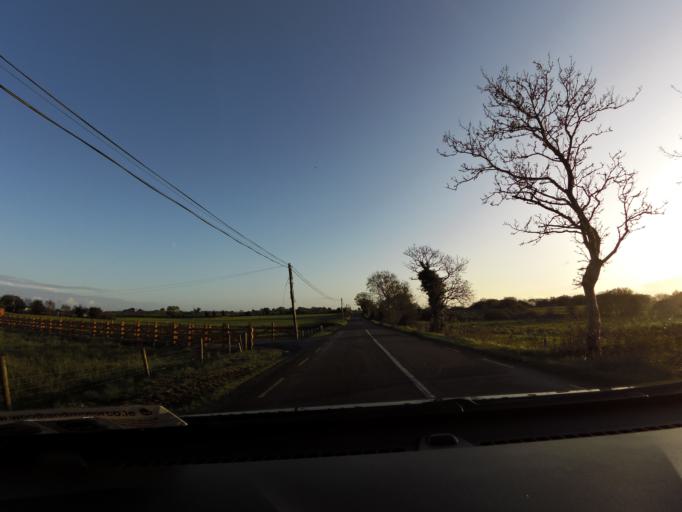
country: IE
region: Connaught
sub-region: Roscommon
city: Castlerea
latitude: 53.7096
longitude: -8.5643
